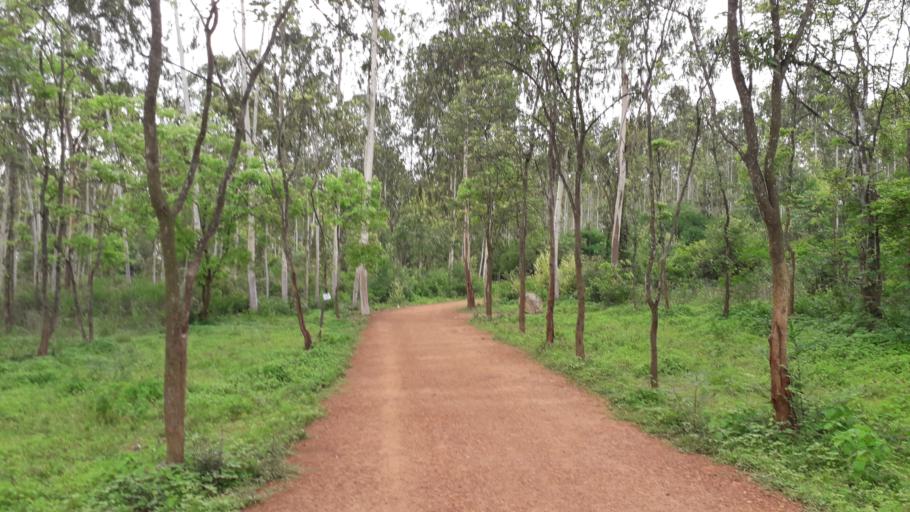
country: IN
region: Andhra Pradesh
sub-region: East Godavari
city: Rajahmundry
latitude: 17.0345
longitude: 81.8227
